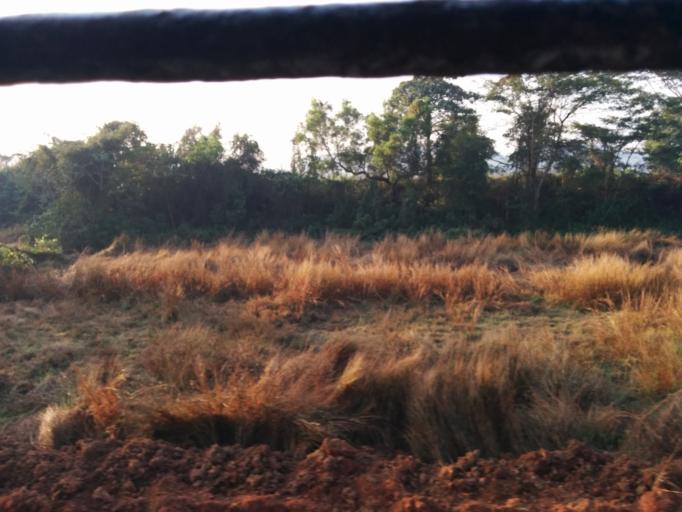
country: IN
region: Goa
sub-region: South Goa
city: Davorlim
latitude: 15.2666
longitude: 73.9965
